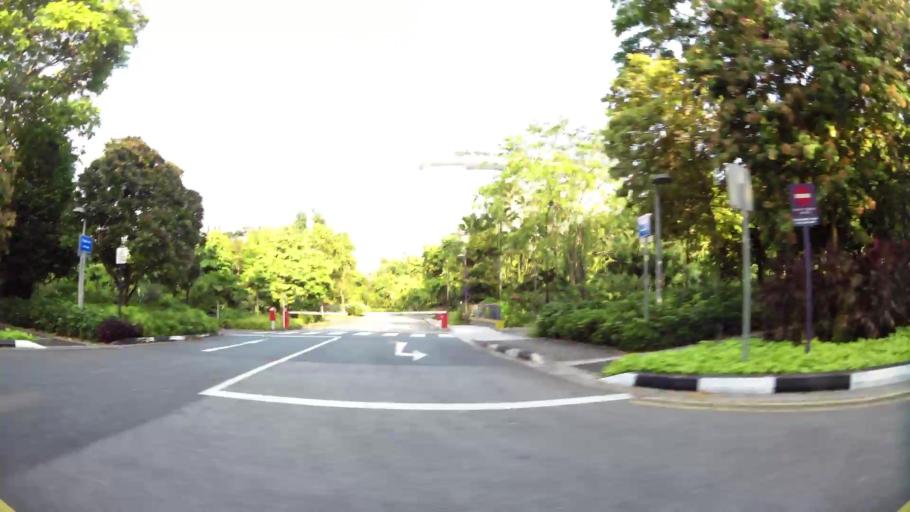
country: SG
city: Singapore
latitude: 1.2795
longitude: 103.8642
